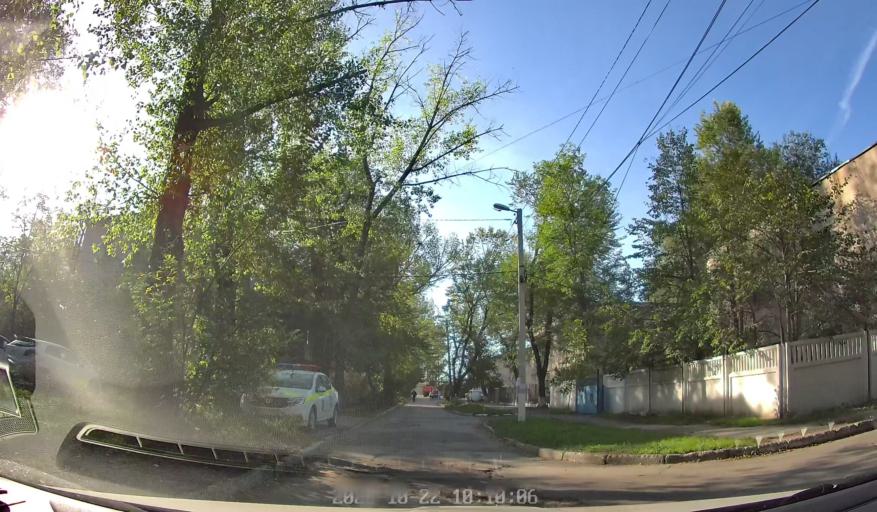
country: MD
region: Chisinau
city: Singera
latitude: 46.9393
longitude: 28.9262
